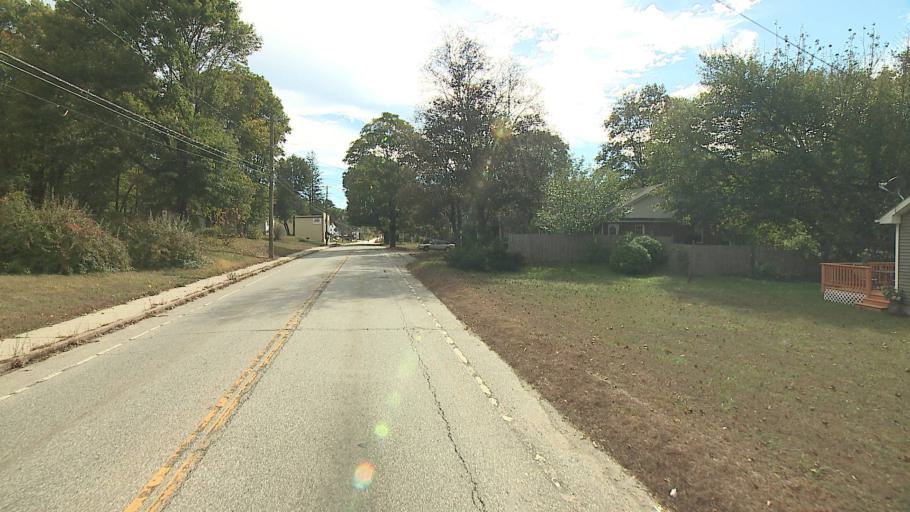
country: US
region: Connecticut
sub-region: Windham County
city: Danielson
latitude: 41.8184
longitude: -71.8776
